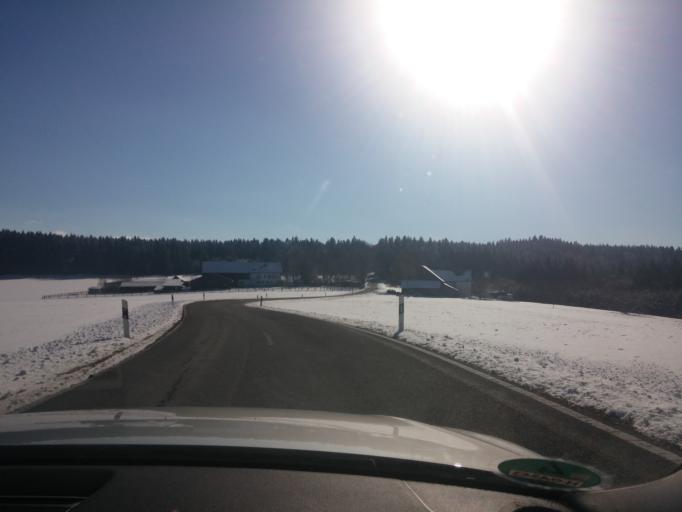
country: DE
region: Baden-Wuerttemberg
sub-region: Tuebingen Region
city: Aichstetten
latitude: 47.8550
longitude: 10.0594
